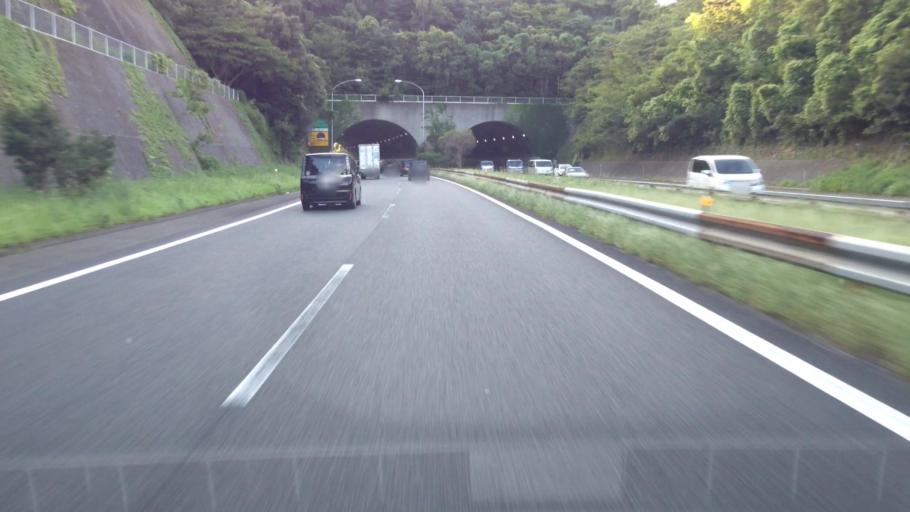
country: JP
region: Kanagawa
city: Zushi
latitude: 35.3218
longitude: 139.6034
